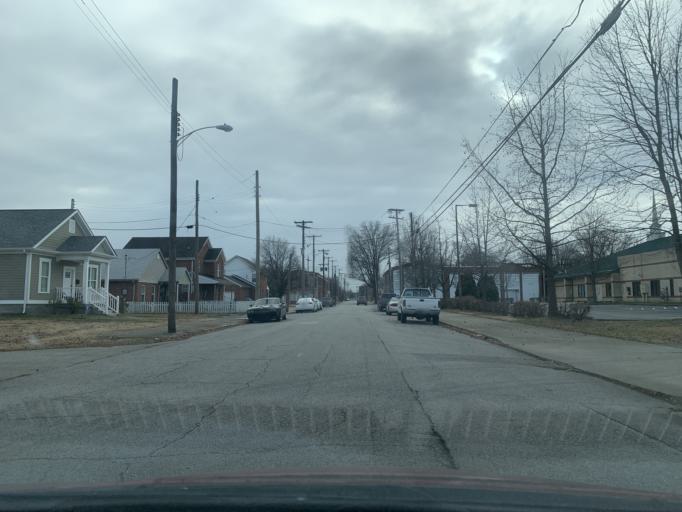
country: US
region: Kentucky
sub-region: Jefferson County
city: Louisville
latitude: 38.2550
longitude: -85.7822
